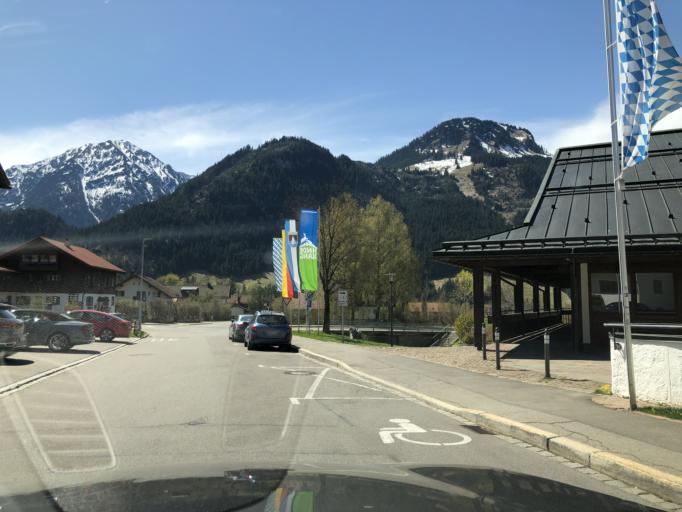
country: AT
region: Tyrol
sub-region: Politischer Bezirk Reutte
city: Schattwald
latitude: 47.5056
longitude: 10.3731
